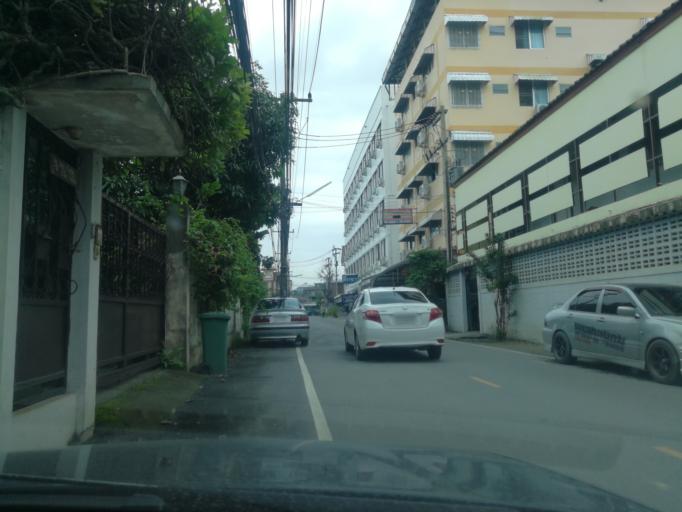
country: TH
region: Chiang Mai
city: Chiang Mai
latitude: 18.8070
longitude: 98.9647
